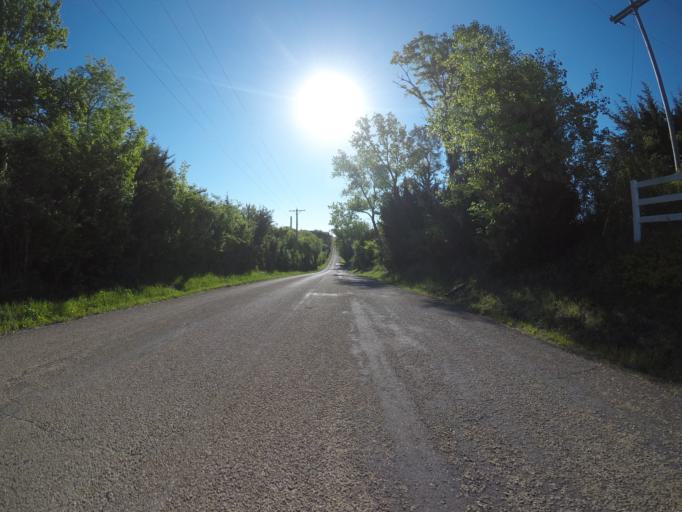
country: US
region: Kansas
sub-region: Shawnee County
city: Topeka
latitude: 39.0150
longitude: -95.5291
